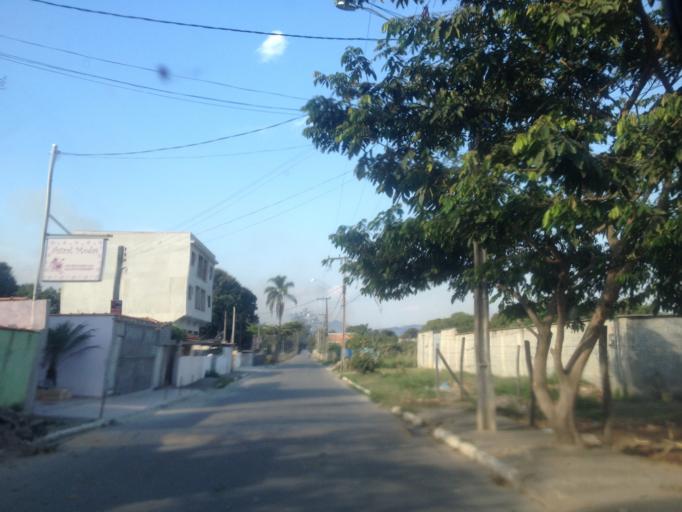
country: BR
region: Rio de Janeiro
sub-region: Porto Real
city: Porto Real
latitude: -22.4117
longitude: -44.2957
